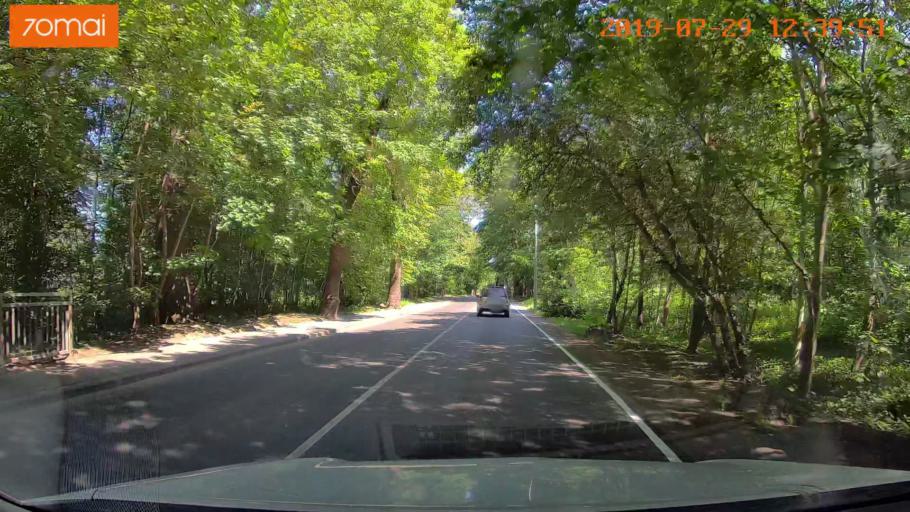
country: RU
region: Kaliningrad
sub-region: Gorod Kaliningrad
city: Kaliningrad
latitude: 54.6645
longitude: 20.5410
